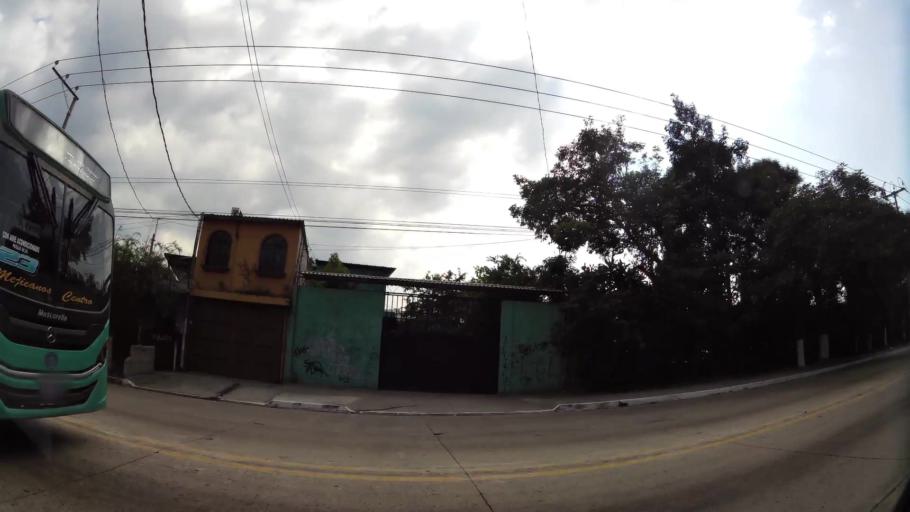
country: SV
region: San Salvador
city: Mejicanos
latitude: 13.7348
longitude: -89.2141
